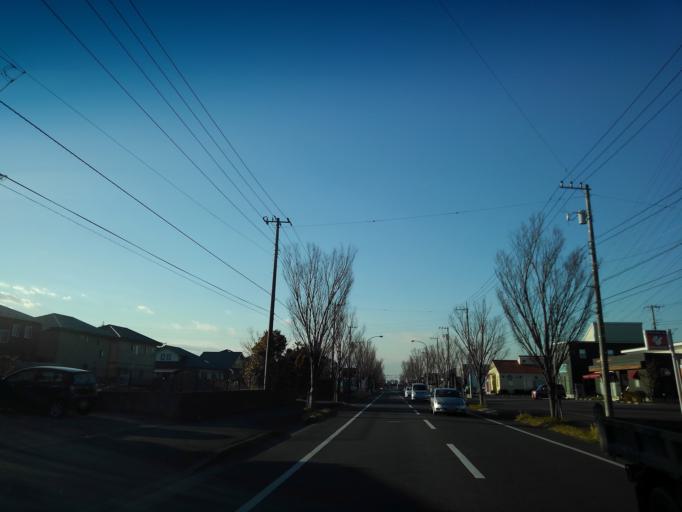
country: JP
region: Chiba
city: Kimitsu
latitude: 35.3111
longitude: 139.9200
